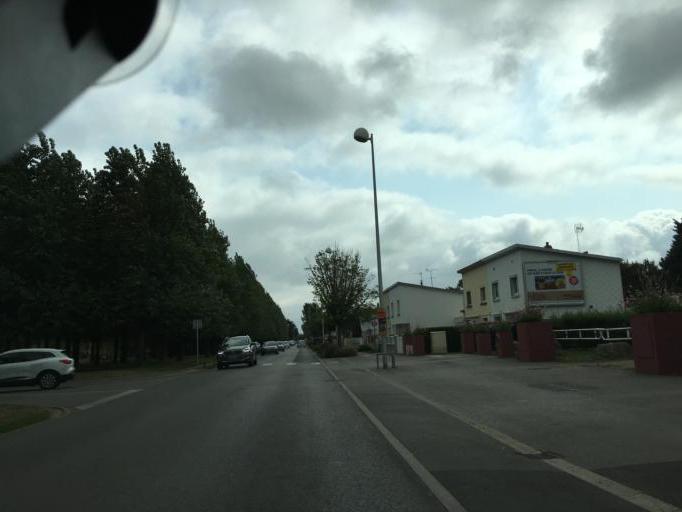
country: FR
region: Nord-Pas-de-Calais
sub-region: Departement du Pas-de-Calais
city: Berck
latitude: 50.4034
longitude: 1.5865
